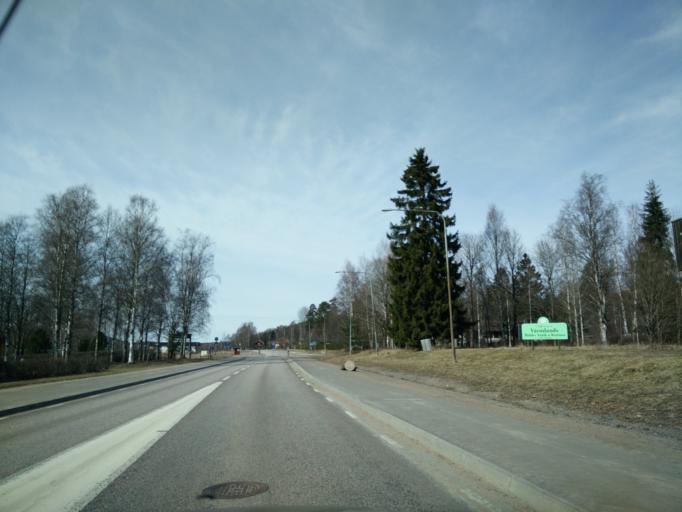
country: SE
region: Vaermland
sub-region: Hagfors Kommun
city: Hagfors
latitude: 60.0245
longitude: 13.6181
